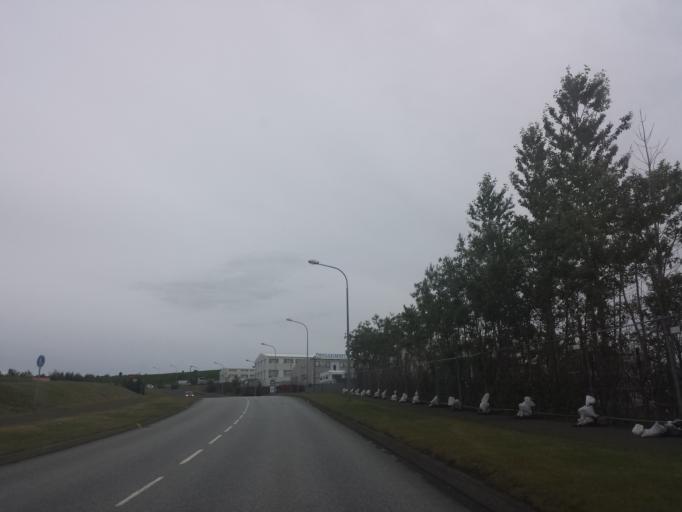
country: IS
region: Capital Region
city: Kopavogur
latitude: 64.0977
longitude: -21.8753
